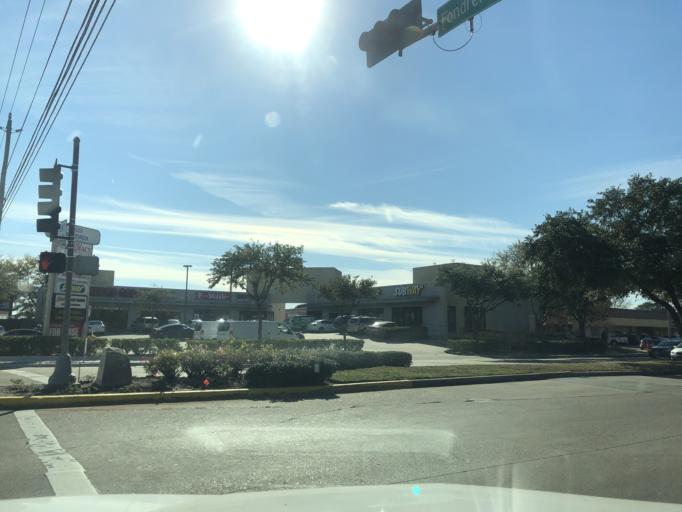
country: US
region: Texas
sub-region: Harris County
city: Bellaire
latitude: 29.6757
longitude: -95.5088
